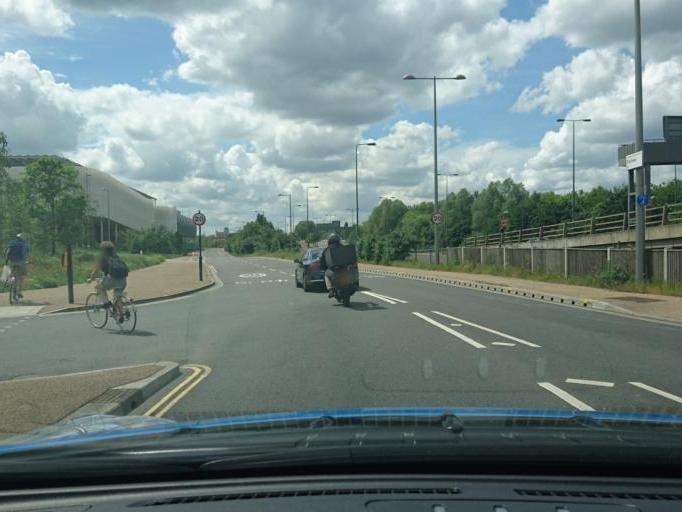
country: GB
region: England
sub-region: Greater London
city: Hackney
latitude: 51.5505
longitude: -0.0224
